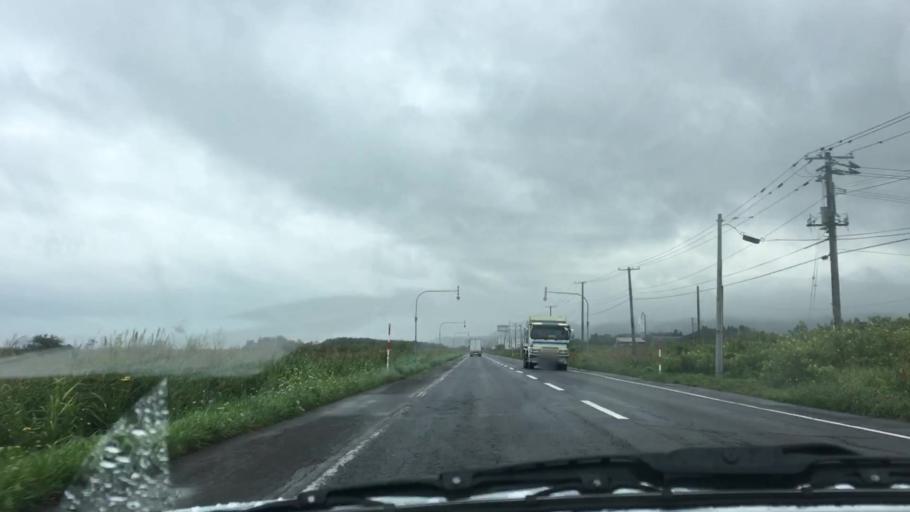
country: JP
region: Hokkaido
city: Niseko Town
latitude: 42.3959
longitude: 140.3010
